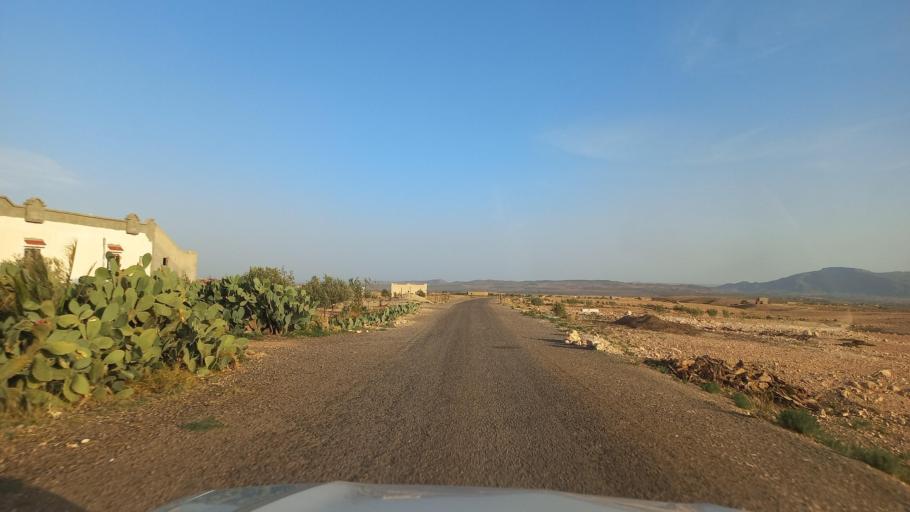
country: TN
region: Al Qasrayn
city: Kasserine
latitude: 35.2760
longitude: 8.9117
